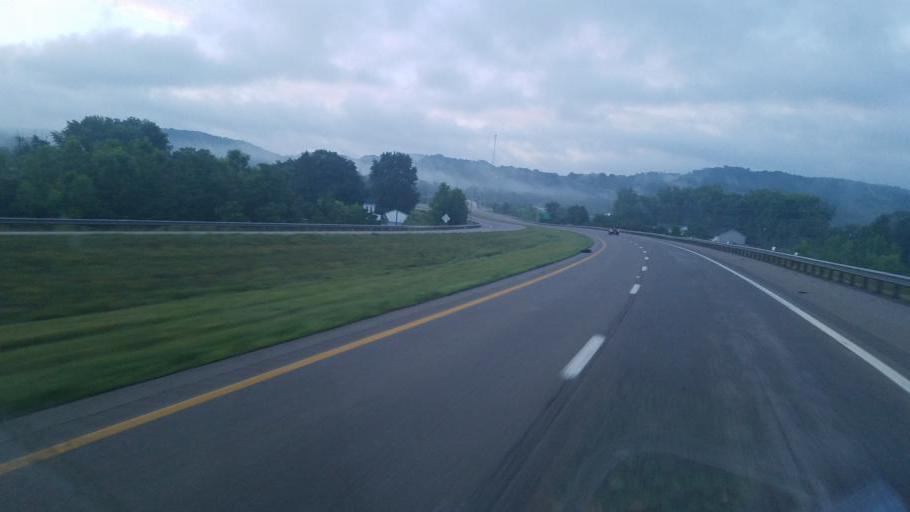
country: US
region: Ohio
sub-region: Pike County
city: Waverly
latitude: 39.2050
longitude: -82.8216
